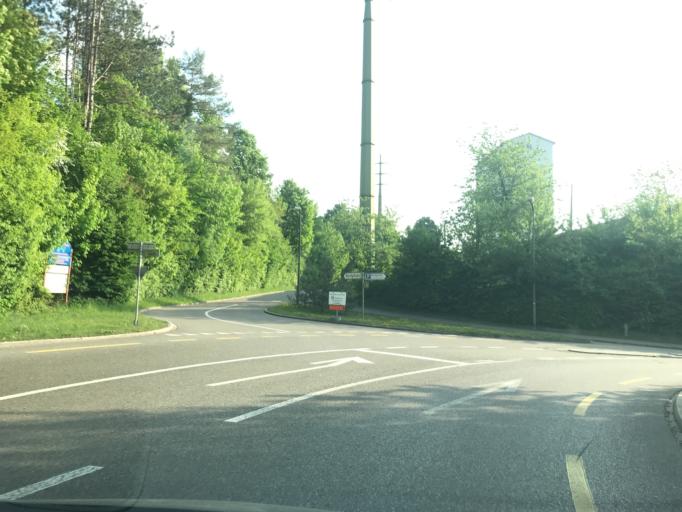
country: CH
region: Zurich
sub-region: Bezirk Winterthur
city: Toess (Kreis 4) / Eichliacker
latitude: 47.4847
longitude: 8.7119
